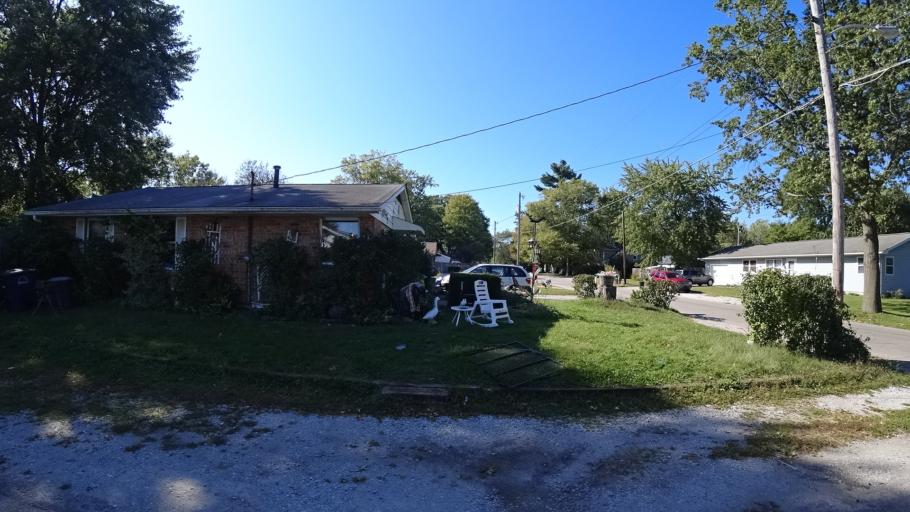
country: US
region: Indiana
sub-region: LaPorte County
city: Michigan City
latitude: 41.6919
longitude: -86.8967
